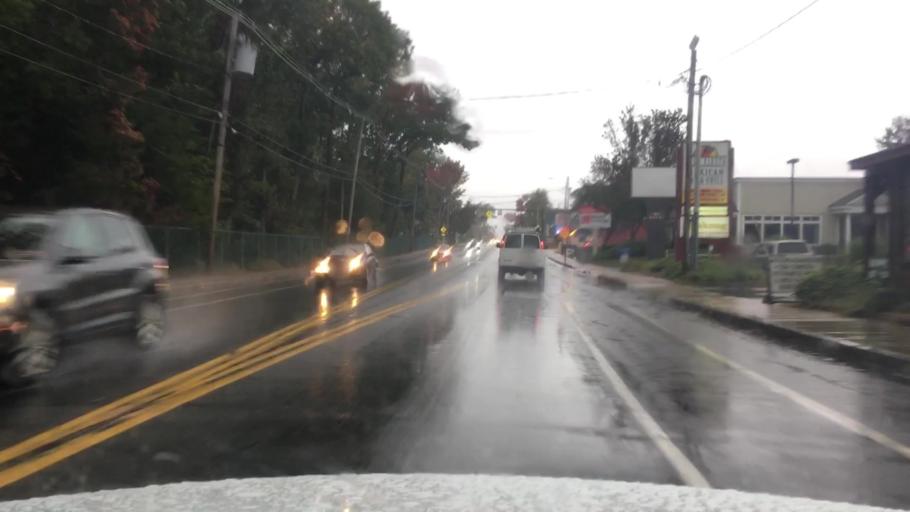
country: US
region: Maine
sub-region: Cumberland County
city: Portland
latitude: 43.6771
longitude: -70.2875
